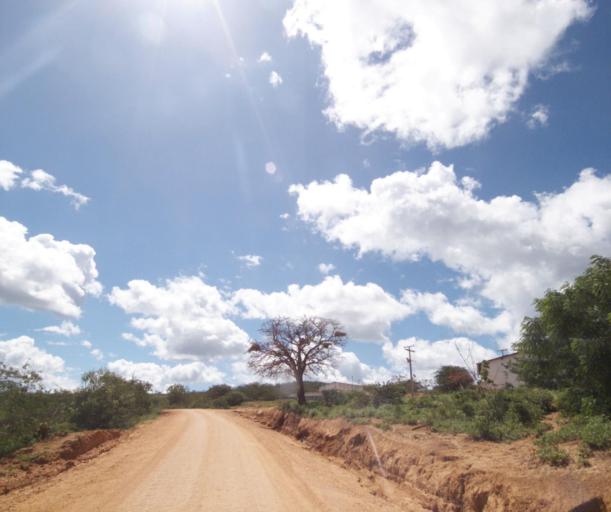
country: BR
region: Bahia
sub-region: Pocoes
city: Pocoes
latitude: -14.2992
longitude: -40.6476
